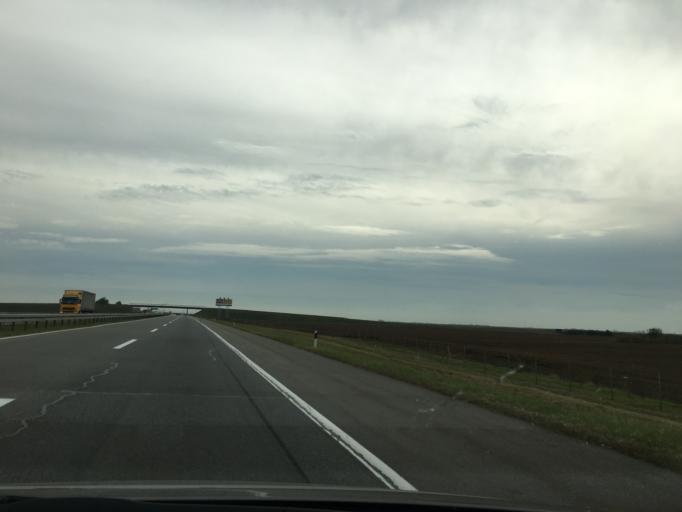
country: RS
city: Krcedin
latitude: 45.1053
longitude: 20.1081
